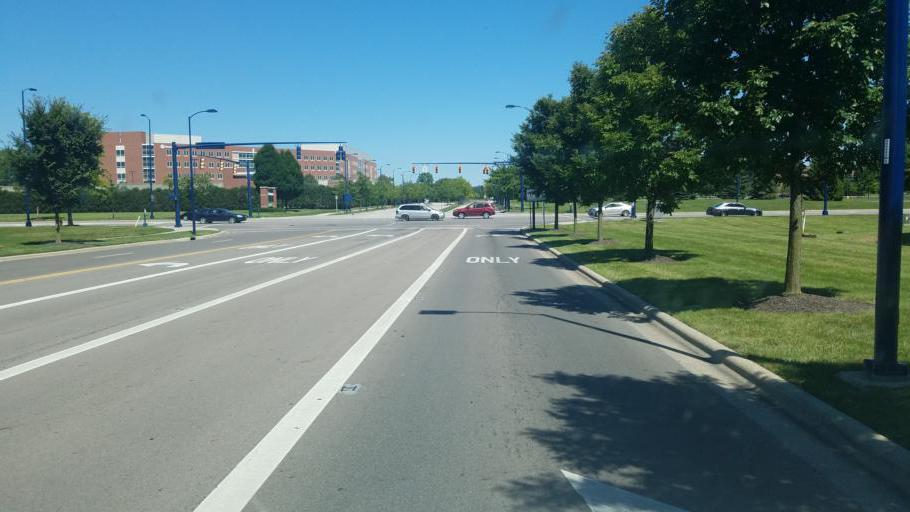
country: US
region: Ohio
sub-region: Franklin County
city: Gahanna
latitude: 40.0423
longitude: -82.9103
